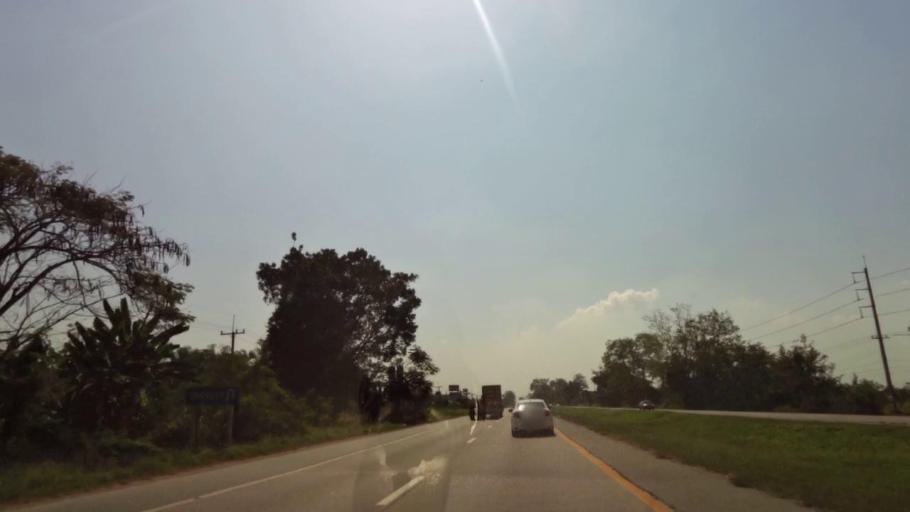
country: TH
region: Phichit
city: Wachira Barami
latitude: 16.6007
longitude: 100.1478
